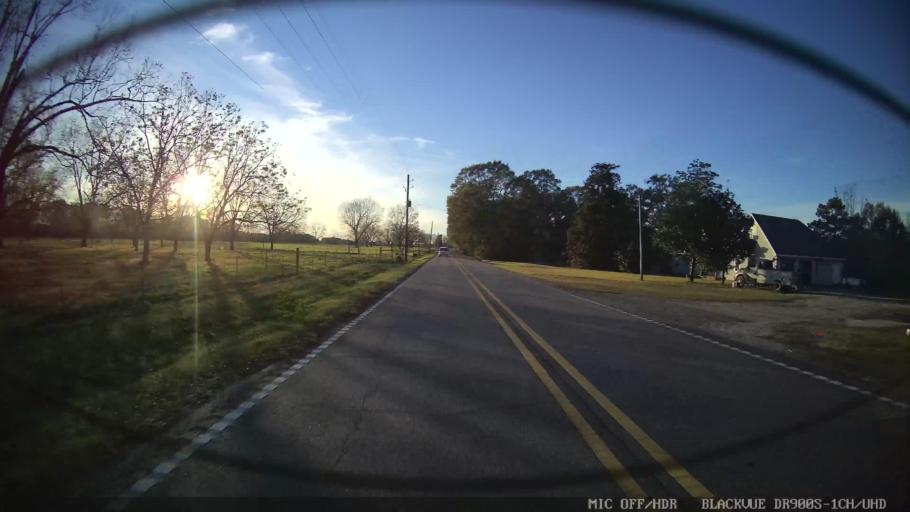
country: US
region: Mississippi
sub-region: Lamar County
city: Lumberton
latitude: 30.9956
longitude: -89.3860
